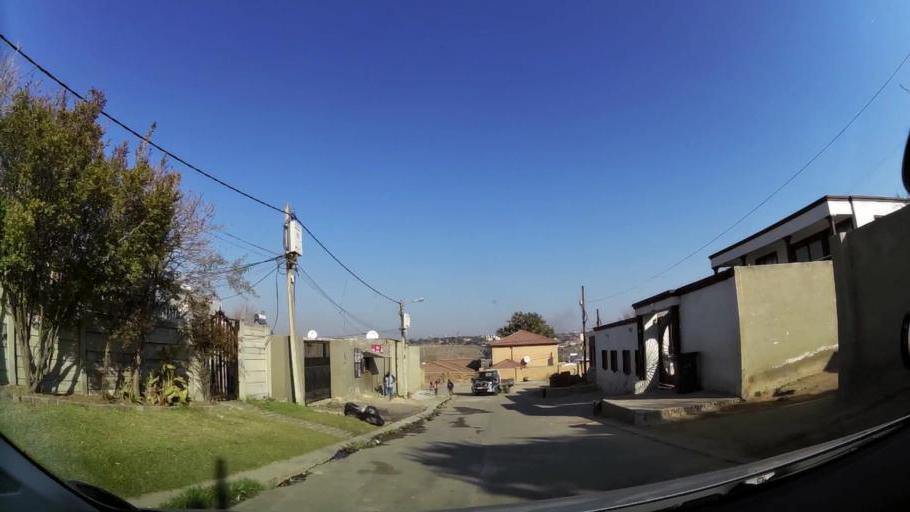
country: ZA
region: Gauteng
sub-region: City of Johannesburg Metropolitan Municipality
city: Modderfontein
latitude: -26.0889
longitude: 28.1126
